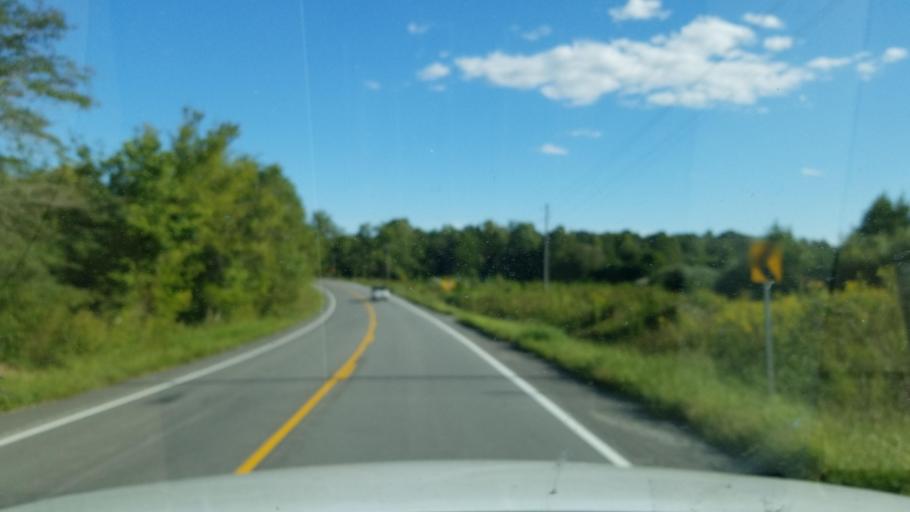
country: US
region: Illinois
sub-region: Hardin County
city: Rosiclare
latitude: 37.5683
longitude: -88.4136
